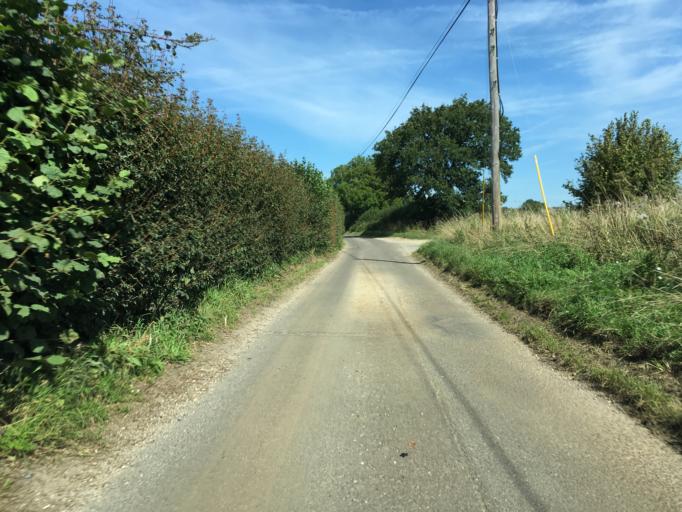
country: GB
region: England
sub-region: Hampshire
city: Highclere
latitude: 51.2968
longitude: -1.3796
